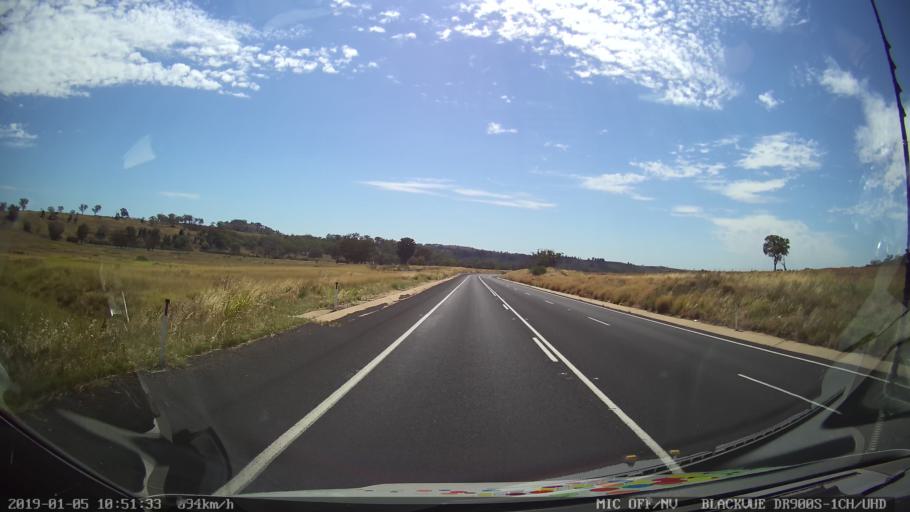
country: AU
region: New South Wales
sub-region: Warrumbungle Shire
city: Coonabarabran
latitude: -31.4249
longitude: 149.0916
